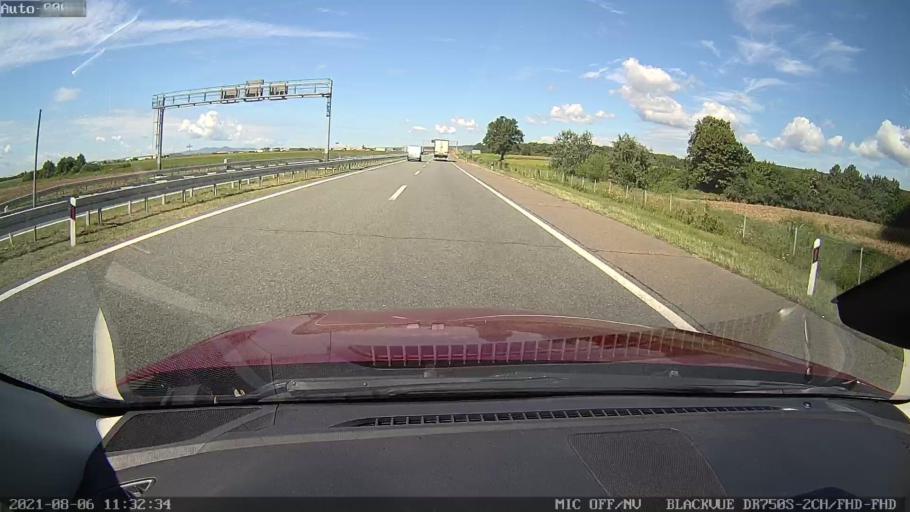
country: HR
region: Brodsko-Posavska
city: Bukovlje
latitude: 45.1755
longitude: 18.0870
